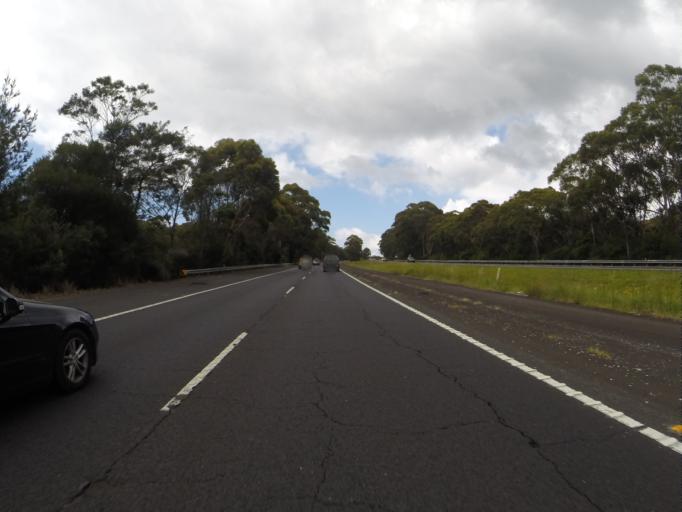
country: AU
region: New South Wales
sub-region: Wollongong
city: Helensburgh
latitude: -34.1999
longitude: 150.9659
